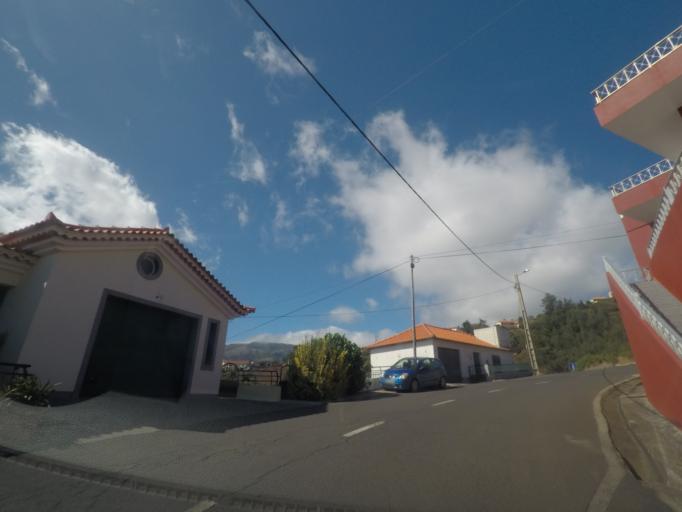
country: PT
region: Madeira
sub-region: Ribeira Brava
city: Campanario
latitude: 32.6918
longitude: -17.0329
